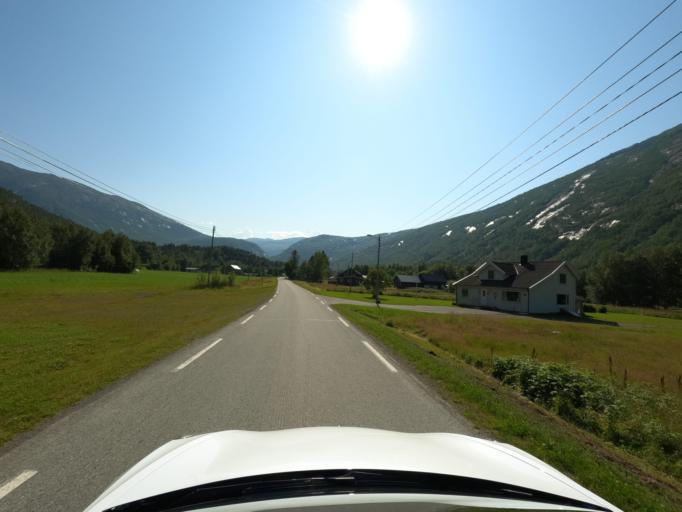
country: NO
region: Nordland
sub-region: Narvik
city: Narvik
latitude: 68.1815
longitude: 17.5539
